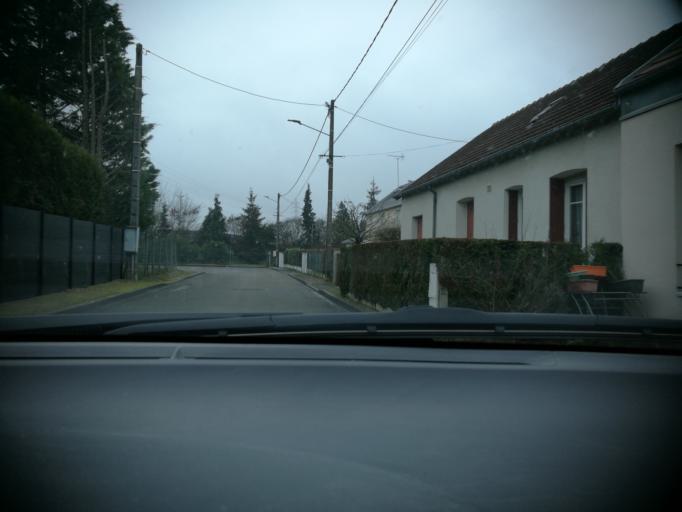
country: FR
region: Centre
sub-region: Departement du Loiret
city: Semoy
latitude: 47.9245
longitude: 1.9439
